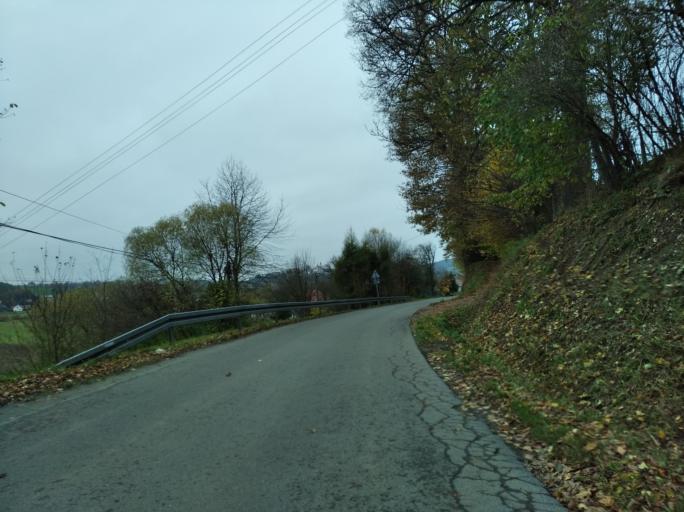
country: PL
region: Subcarpathian Voivodeship
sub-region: Powiat strzyzowski
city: Frysztak
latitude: 49.8296
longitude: 21.6333
